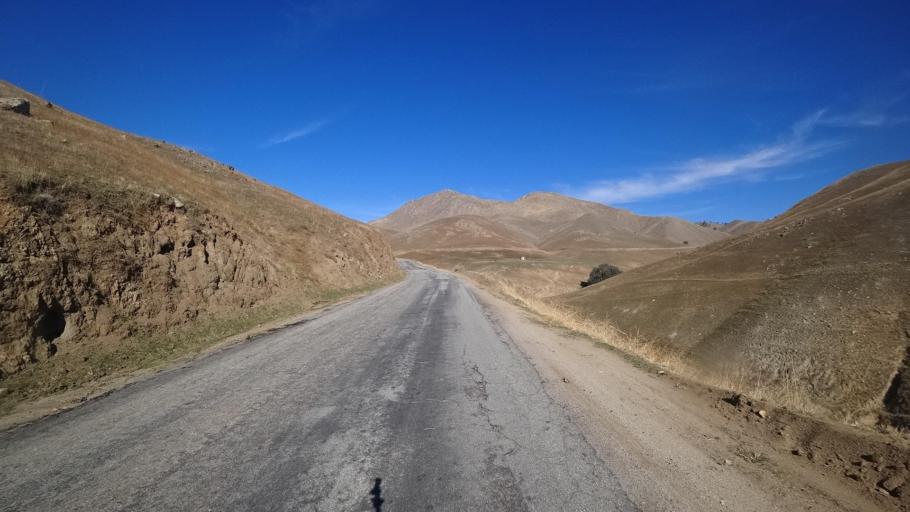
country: US
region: California
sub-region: Kern County
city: Arvin
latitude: 35.4143
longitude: -118.7471
